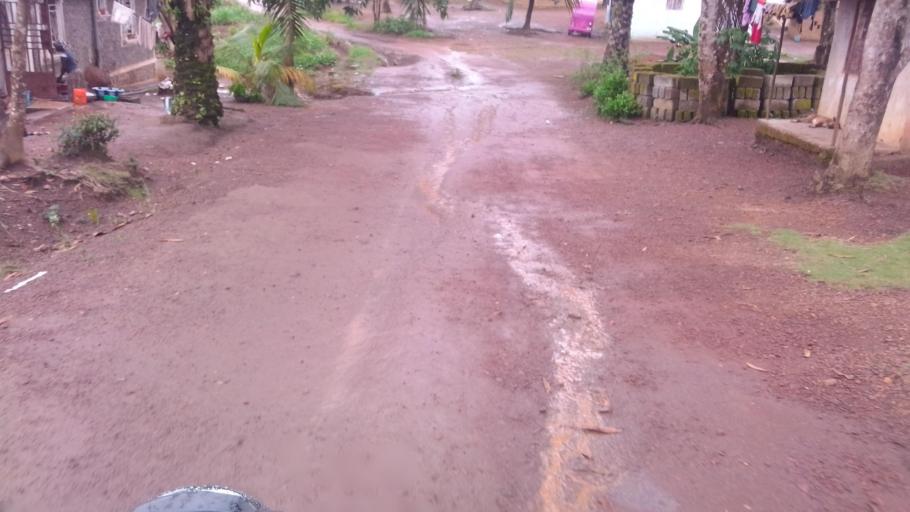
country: SL
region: Eastern Province
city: Kenema
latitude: 7.8499
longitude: -11.1823
